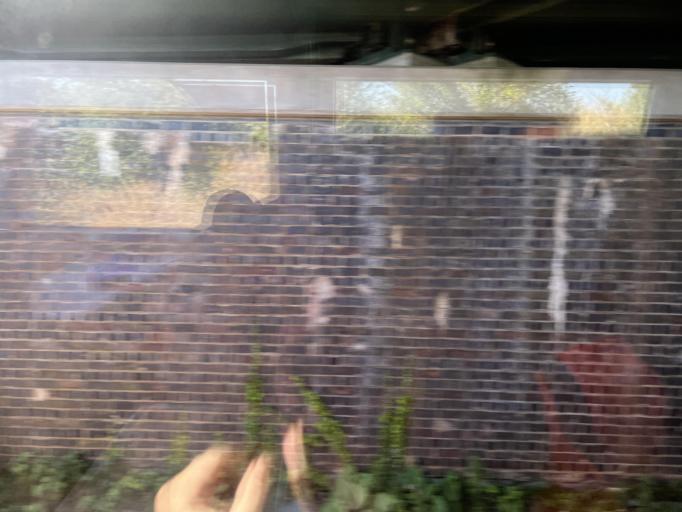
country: GB
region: England
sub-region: Lincolnshire
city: Sleaford
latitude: 52.9939
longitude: -0.3881
